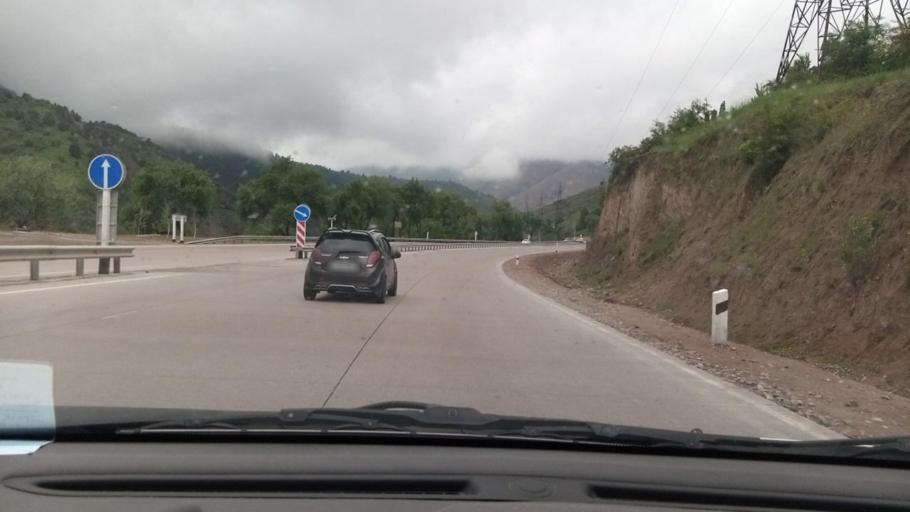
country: UZ
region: Toshkent
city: Angren
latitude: 41.1337
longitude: 70.4631
